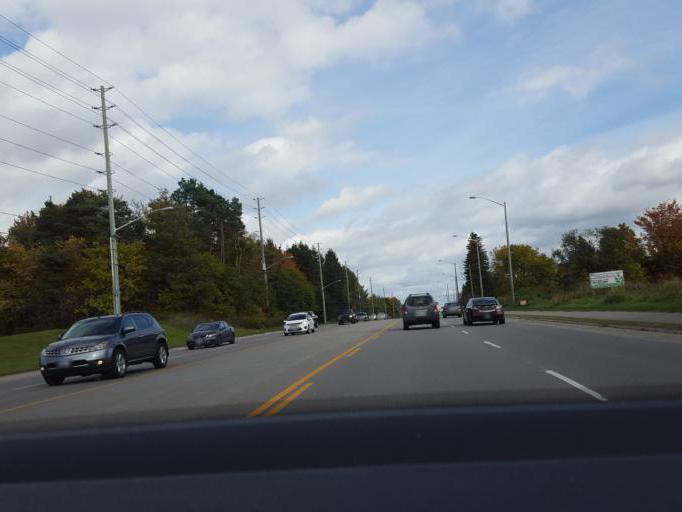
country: CA
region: Ontario
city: Ajax
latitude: 43.8897
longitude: -79.0662
